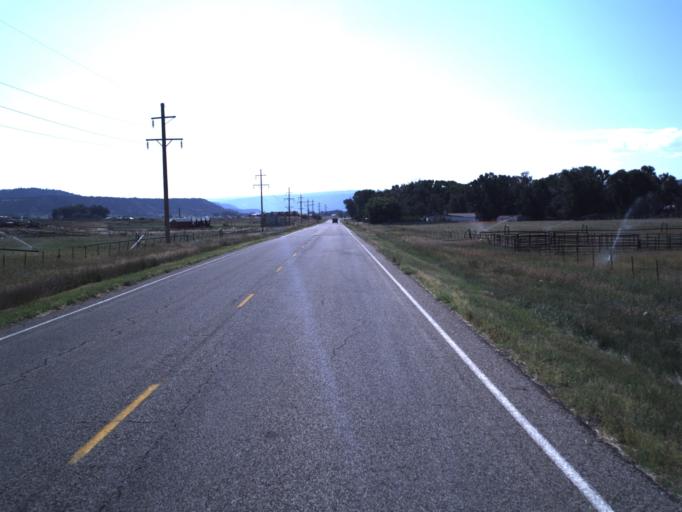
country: US
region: Utah
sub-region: Duchesne County
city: Duchesne
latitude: 40.3773
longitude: -110.7338
